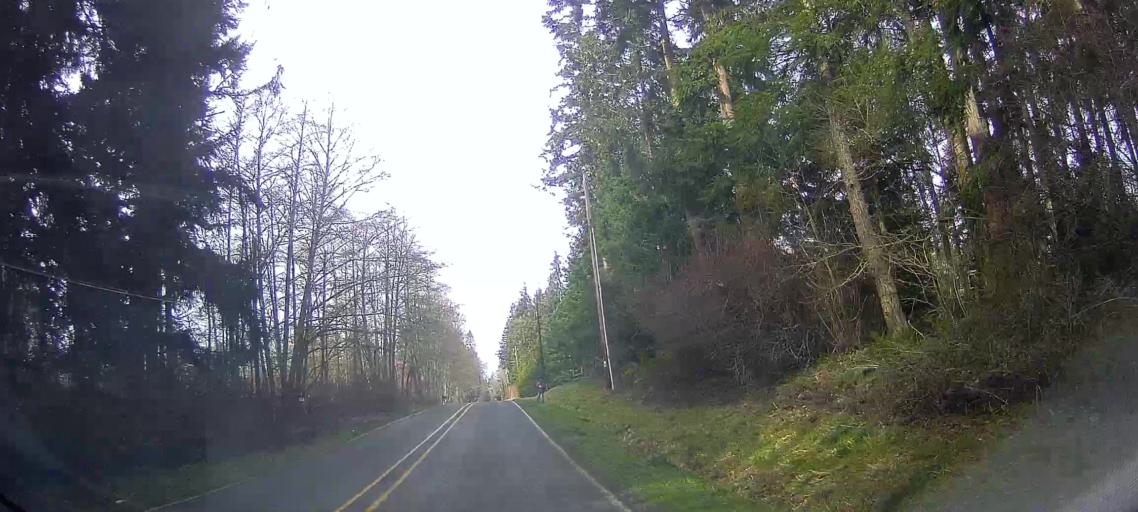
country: US
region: Washington
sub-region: Island County
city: Langley
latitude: 48.0747
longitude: -122.3730
